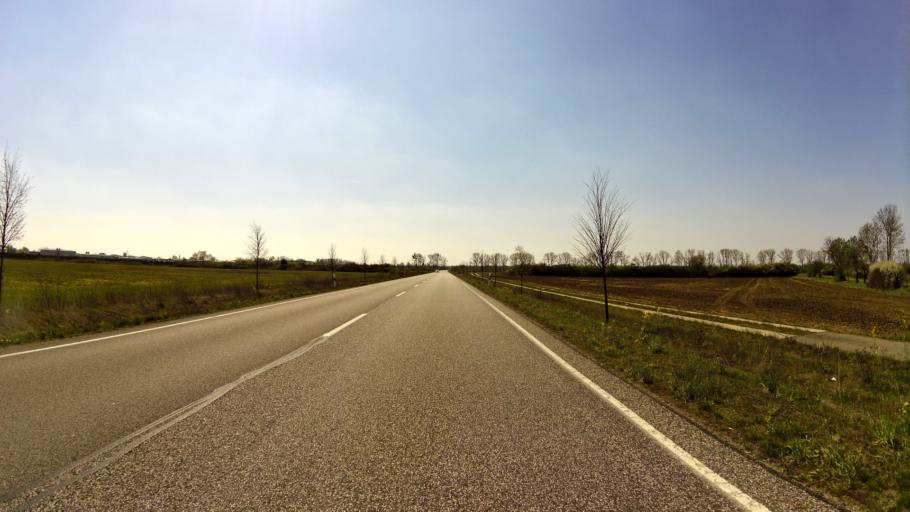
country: DE
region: Saxony-Anhalt
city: Oebisfelde
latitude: 52.4423
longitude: 10.9711
